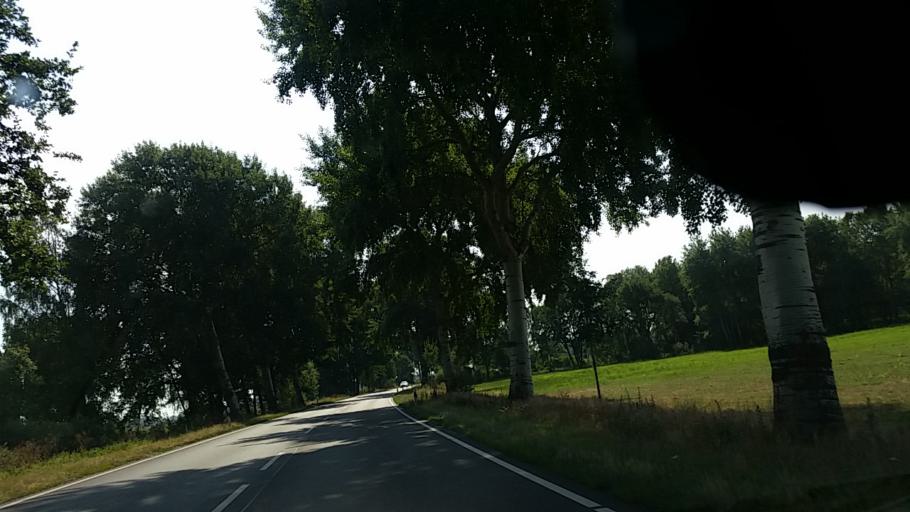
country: DE
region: Lower Saxony
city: Diepholz
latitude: 52.6137
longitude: 8.3145
